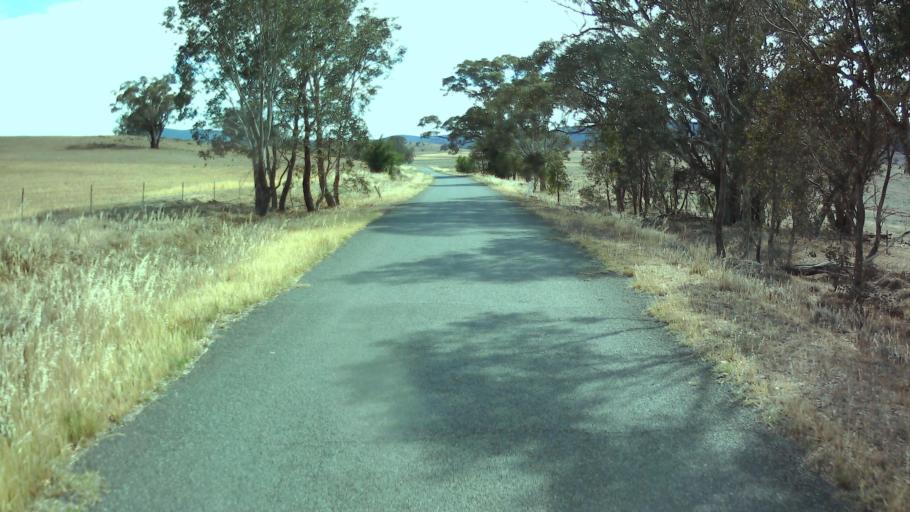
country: AU
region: New South Wales
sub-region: Weddin
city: Grenfell
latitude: -33.8265
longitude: 148.2857
